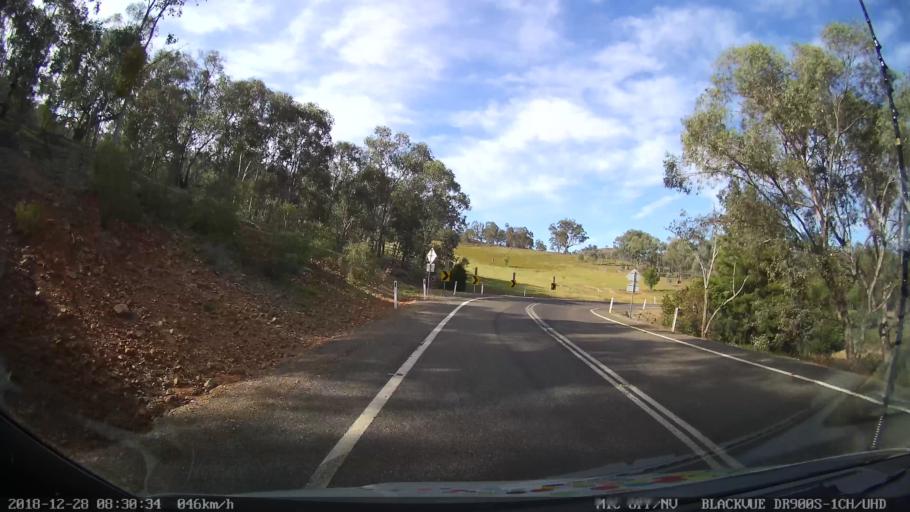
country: AU
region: New South Wales
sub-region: Blayney
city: Blayney
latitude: -33.9566
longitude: 149.3242
